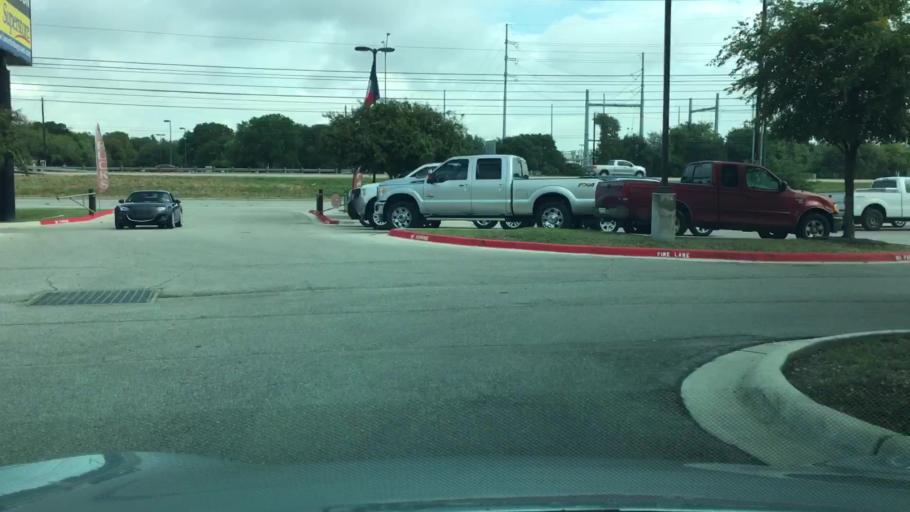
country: US
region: Texas
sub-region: Travis County
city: Austin
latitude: 30.2129
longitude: -97.7248
